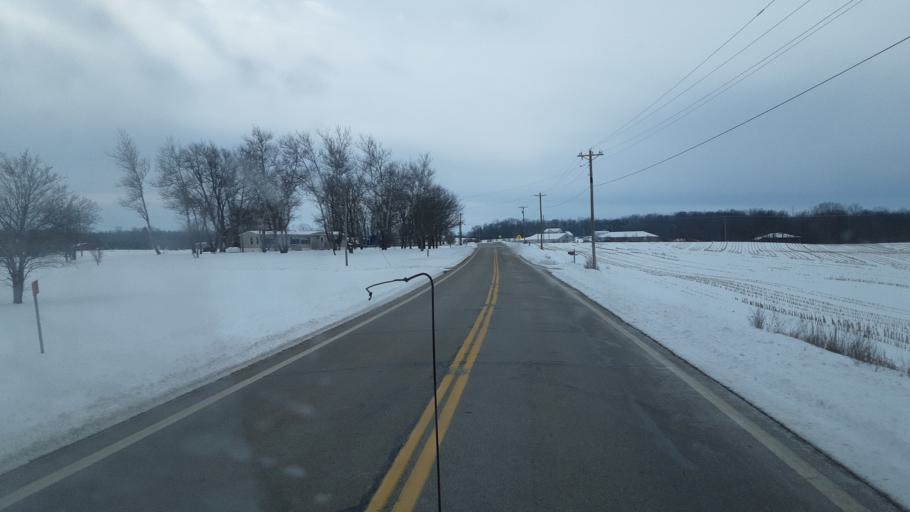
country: US
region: Ohio
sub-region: Champaign County
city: Mechanicsburg
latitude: 40.0429
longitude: -83.5370
